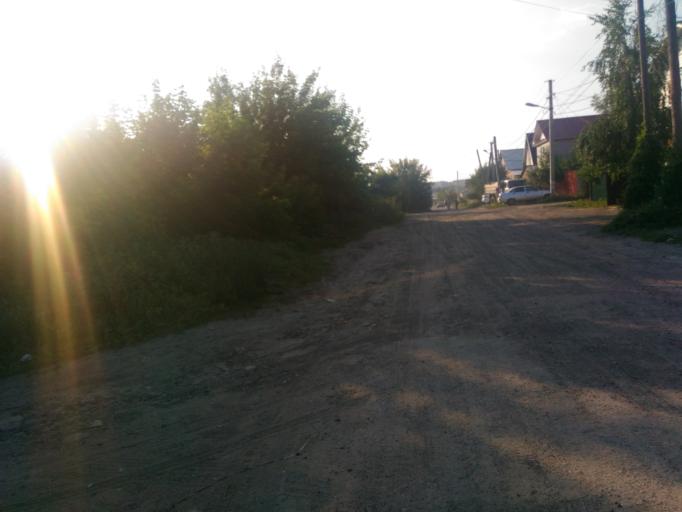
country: RU
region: Ulyanovsk
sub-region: Ulyanovskiy Rayon
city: Ulyanovsk
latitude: 54.3378
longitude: 48.3644
